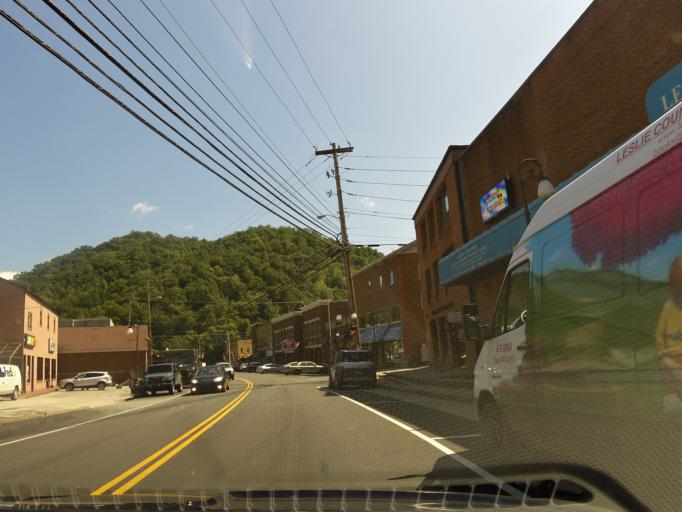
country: US
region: Kentucky
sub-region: Leslie County
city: Hyden
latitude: 37.1621
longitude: -83.3750
